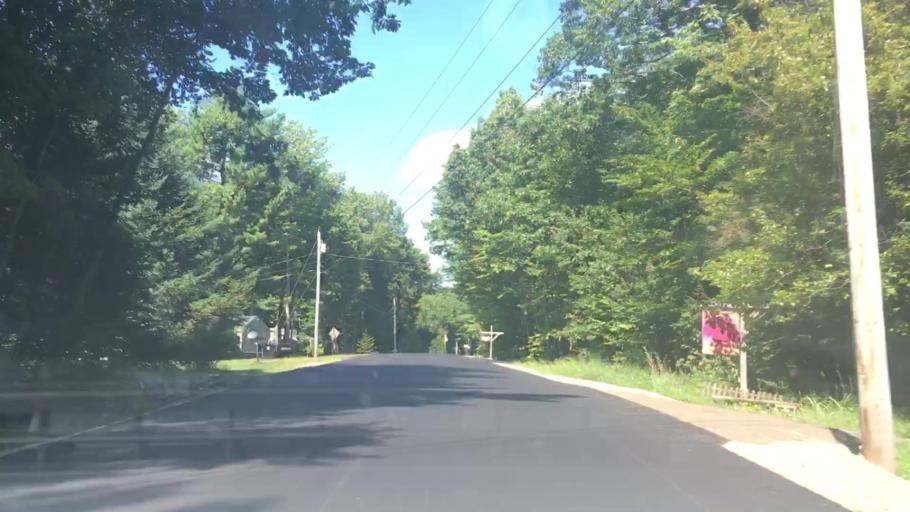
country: US
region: Maine
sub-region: Androscoggin County
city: Sabattus
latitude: 44.1307
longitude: -70.0190
